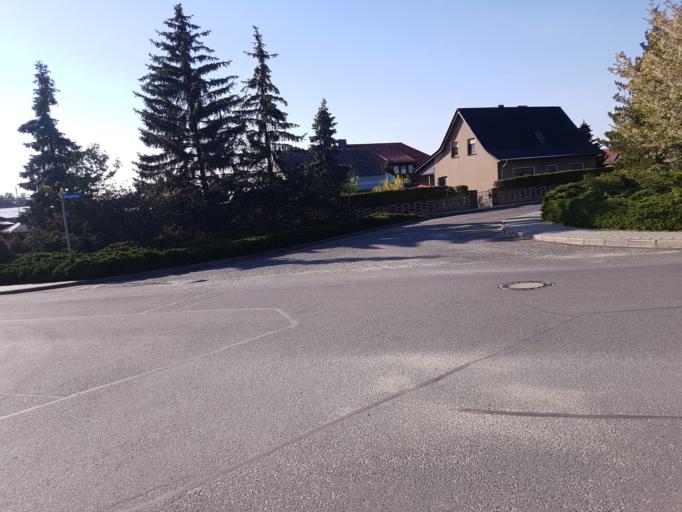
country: DE
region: Brandenburg
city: Groden
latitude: 51.4019
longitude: 13.5681
